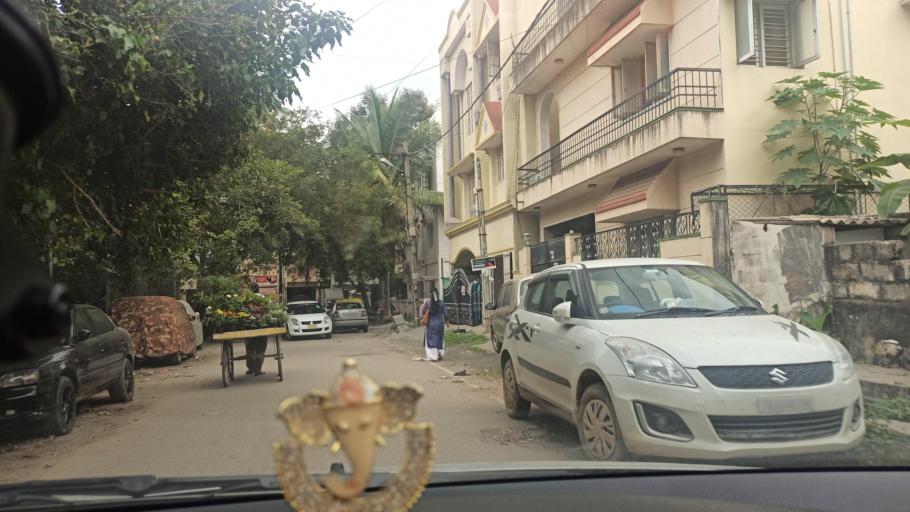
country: IN
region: Karnataka
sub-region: Bangalore Urban
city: Bangalore
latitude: 12.9203
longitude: 77.6474
